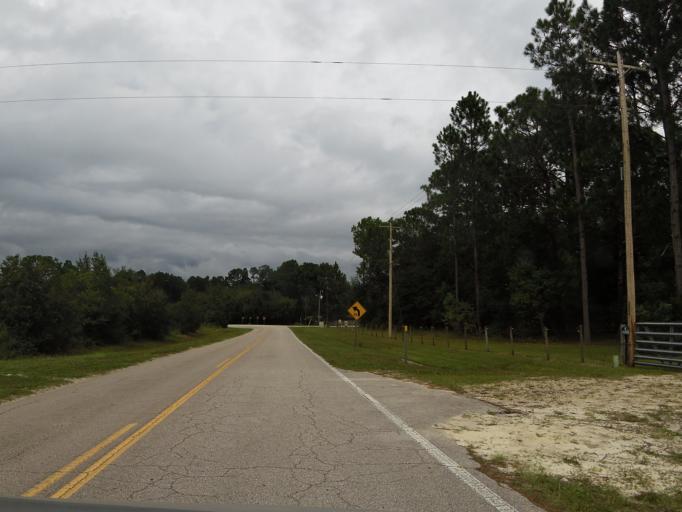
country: US
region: Florida
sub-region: Clay County
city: Middleburg
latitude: 30.1248
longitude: -81.9618
